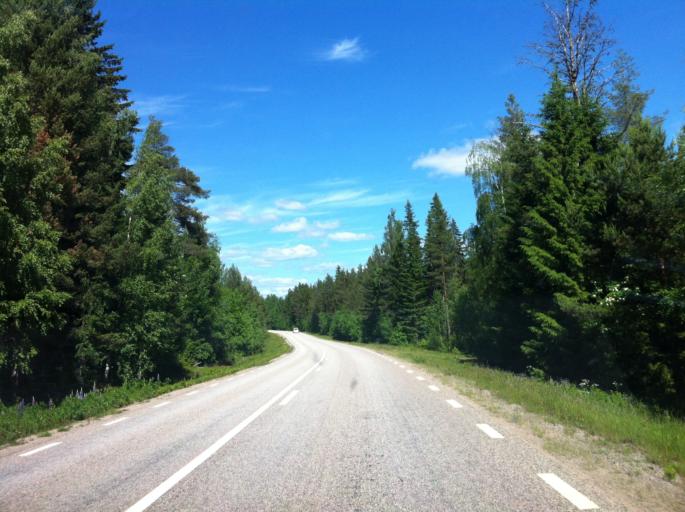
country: SE
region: Gaevleborg
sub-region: Ljusdals Kommun
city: Farila
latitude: 61.9835
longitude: 15.1354
